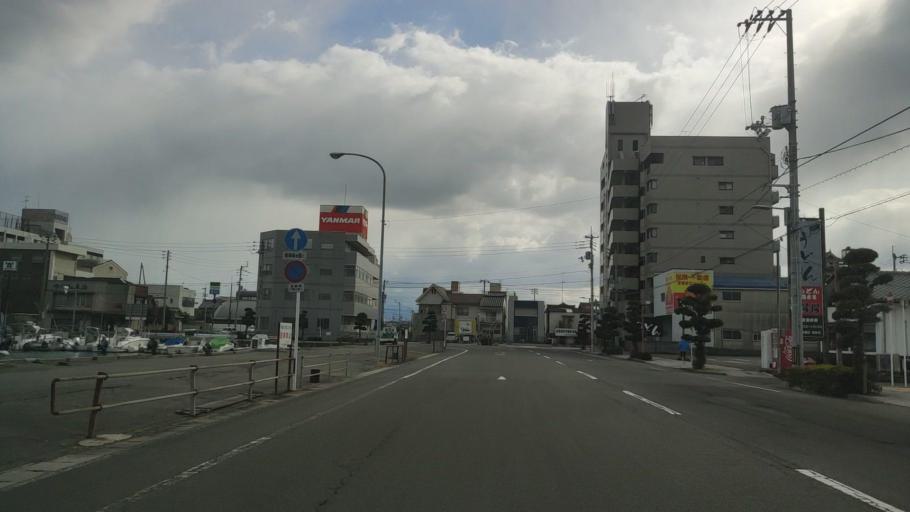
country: JP
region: Ehime
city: Saijo
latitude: 34.0664
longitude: 133.0062
